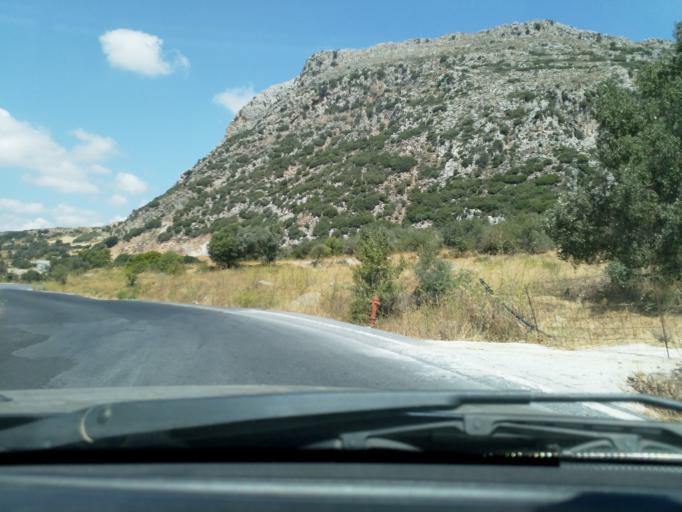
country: GR
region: Crete
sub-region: Nomos Rethymnis
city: Agia Foteini
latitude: 35.2021
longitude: 24.5437
